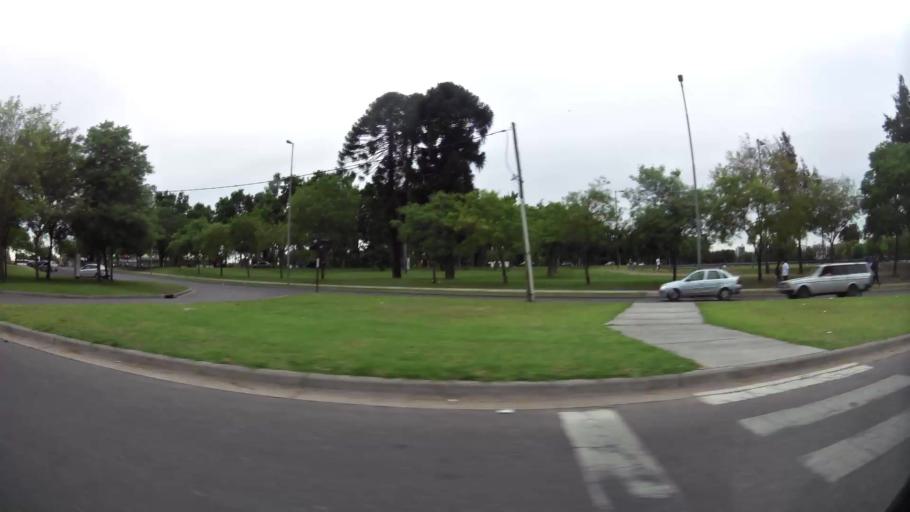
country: AR
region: Santa Fe
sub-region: Departamento de Rosario
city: Rosario
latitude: -32.9090
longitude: -60.6806
